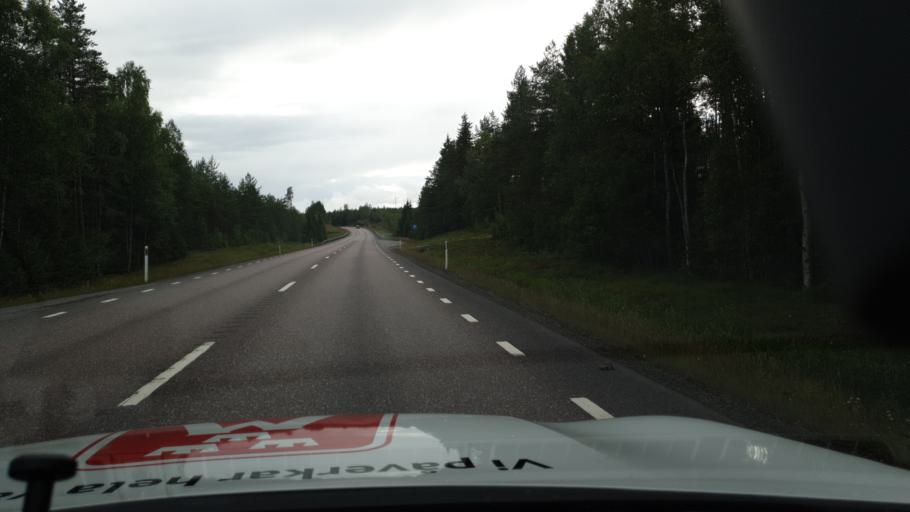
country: SE
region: Vaesterbotten
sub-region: Skelleftea Kommun
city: Burea
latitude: 64.3194
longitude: 21.1756
